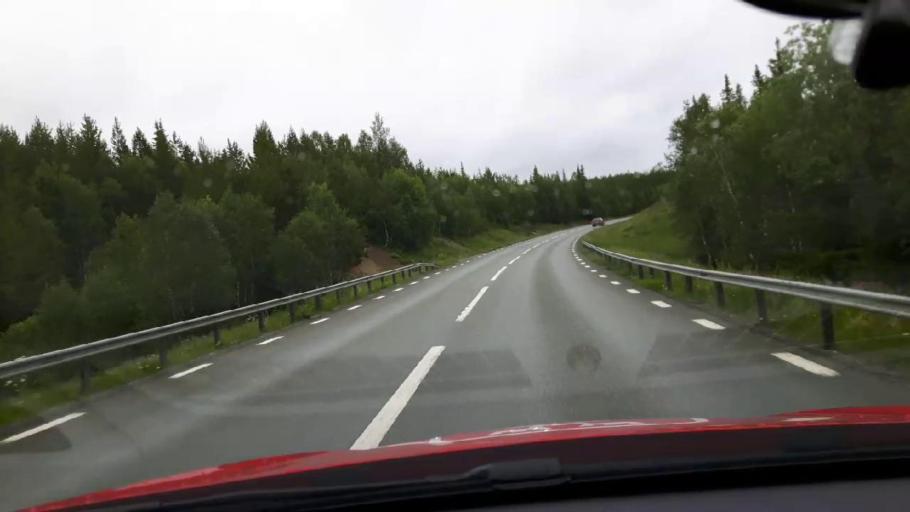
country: SE
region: Jaemtland
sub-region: Are Kommun
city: Are
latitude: 63.2976
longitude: 12.4115
